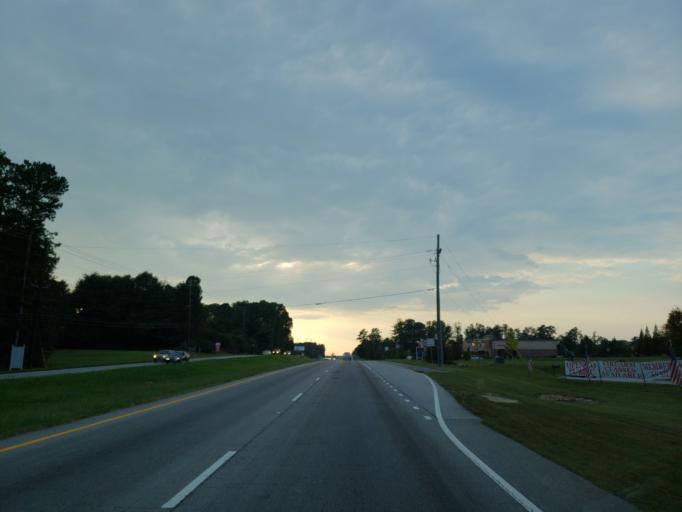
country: US
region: Georgia
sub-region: Paulding County
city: Hiram
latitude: 33.8806
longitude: -84.7205
